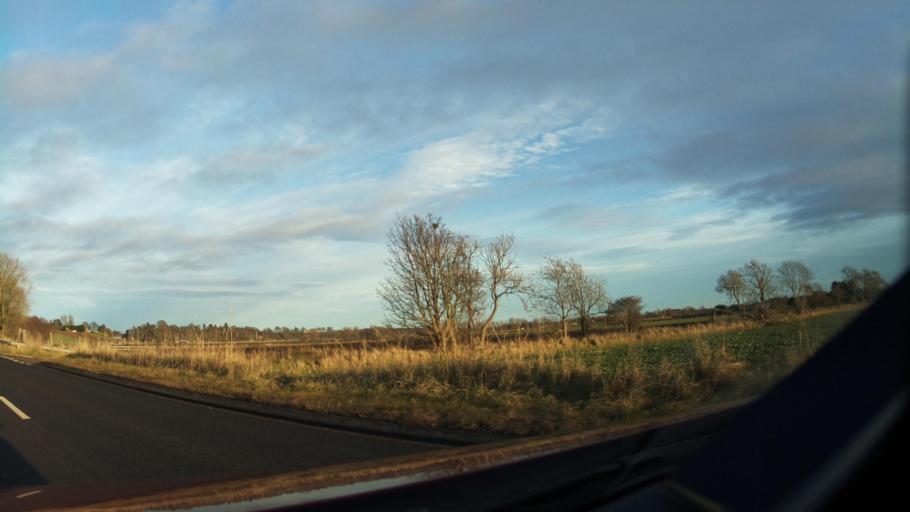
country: GB
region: Scotland
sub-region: Fife
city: Tayport
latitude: 56.4901
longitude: -2.8055
